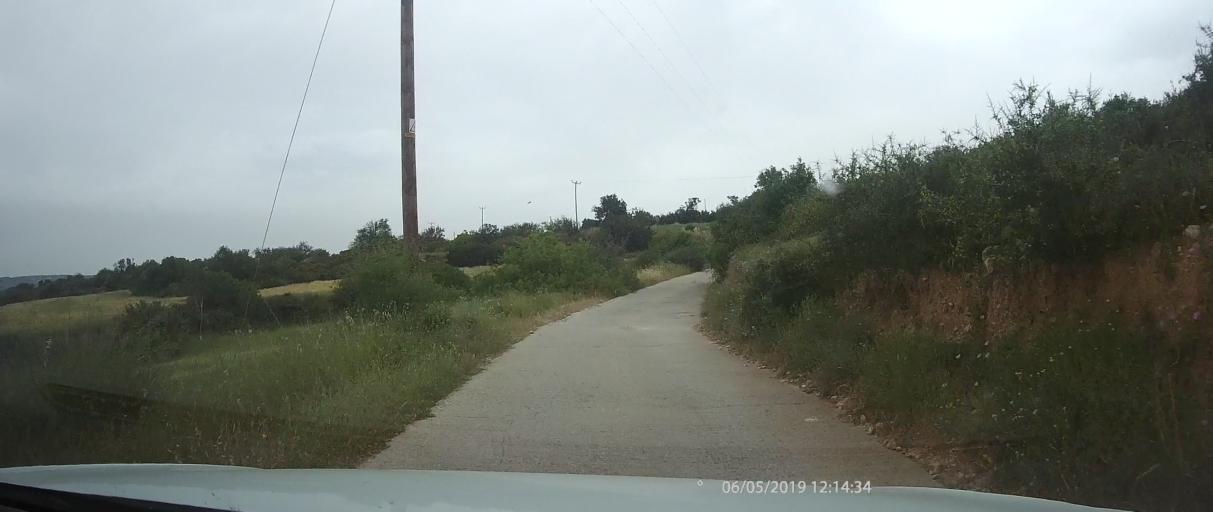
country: CY
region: Pafos
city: Tala
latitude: 34.8472
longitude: 32.4222
